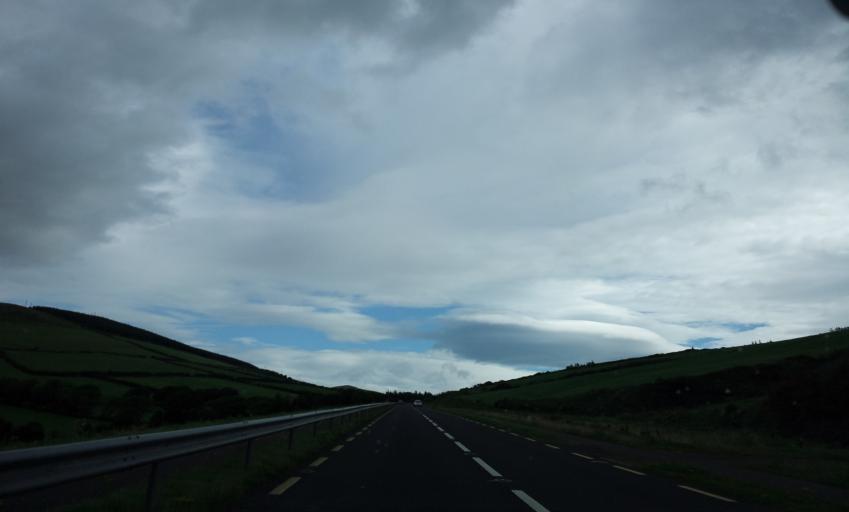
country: IE
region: Munster
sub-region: Ciarrai
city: Killorglin
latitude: 52.1654
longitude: -10.0121
